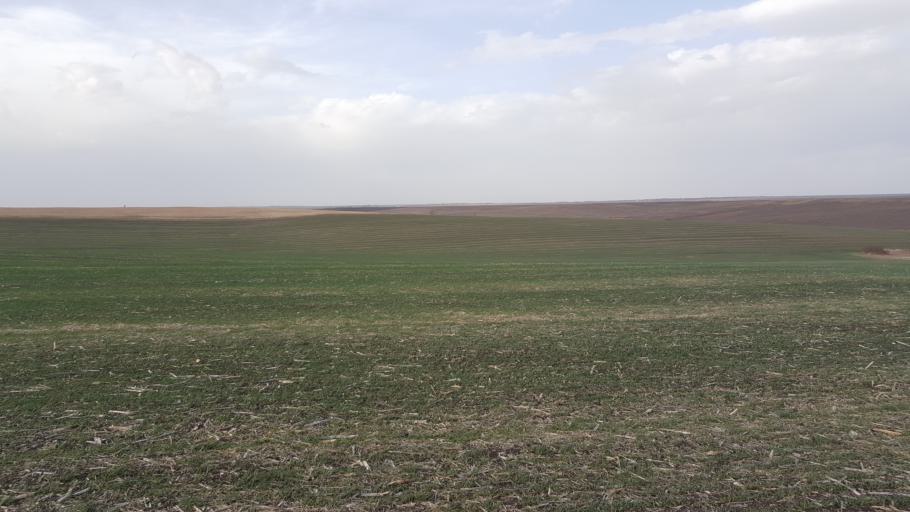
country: BG
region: Stara Zagora
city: Gulubovo
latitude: 42.1417
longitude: 25.7464
